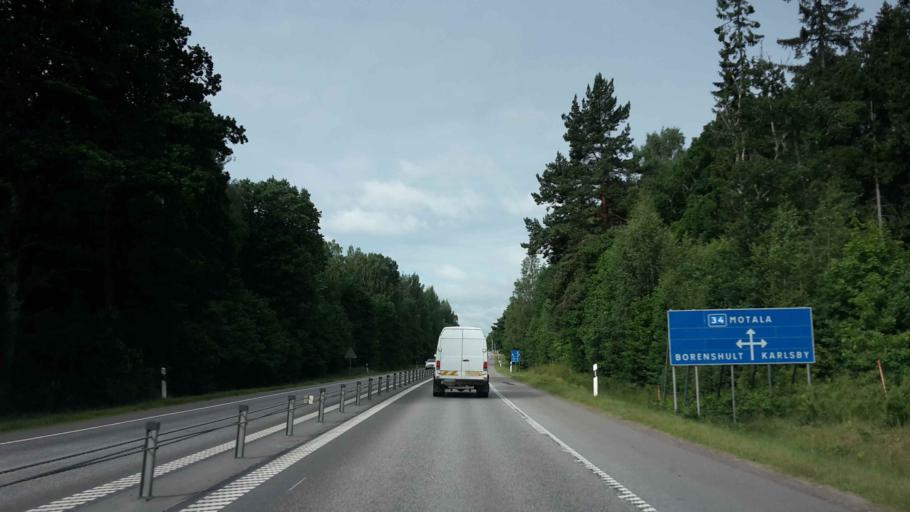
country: SE
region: OEstergoetland
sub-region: Motala Kommun
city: Motala
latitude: 58.5793
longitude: 15.1022
